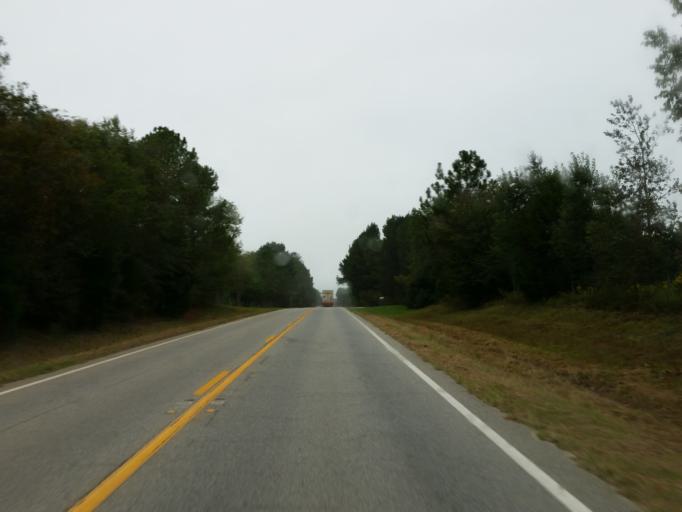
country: US
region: Georgia
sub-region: Berrien County
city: Ray City
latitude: 31.1118
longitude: -83.2977
